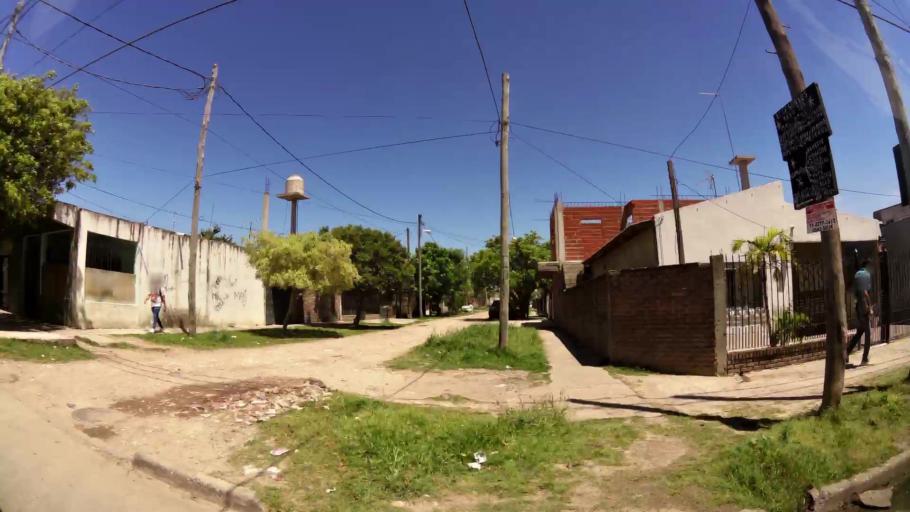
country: AR
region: Buenos Aires
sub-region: Partido de Quilmes
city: Quilmes
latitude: -34.7198
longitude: -58.3219
